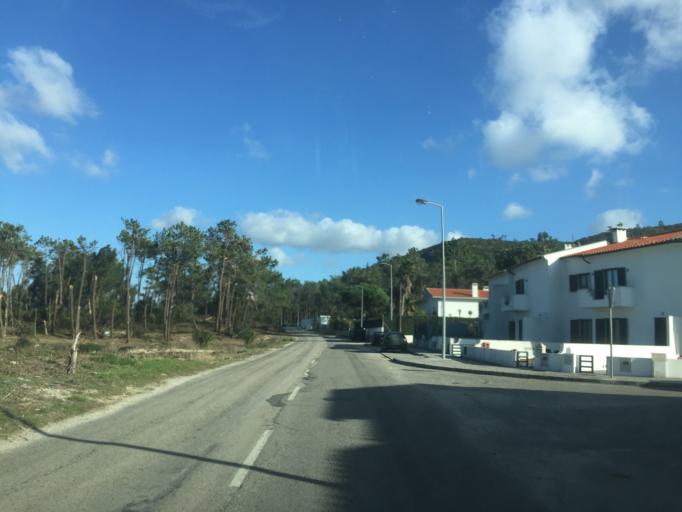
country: PT
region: Coimbra
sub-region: Figueira da Foz
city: Buarcos
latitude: 40.2155
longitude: -8.8876
